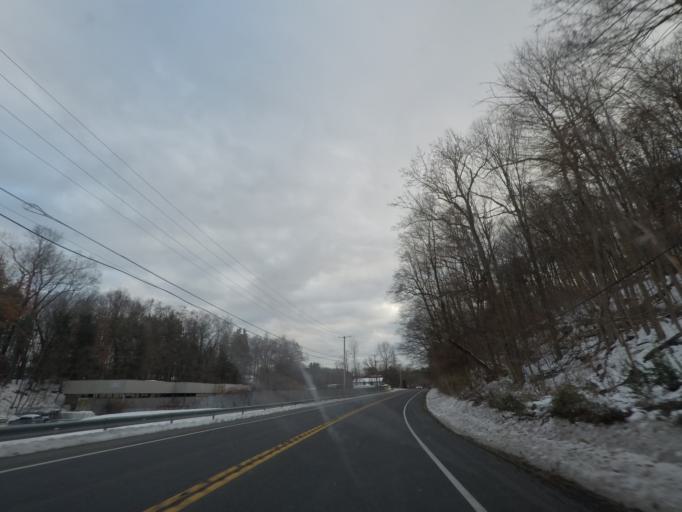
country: US
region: New York
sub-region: Ulster County
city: Rosendale Village
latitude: 41.8817
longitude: -74.0472
